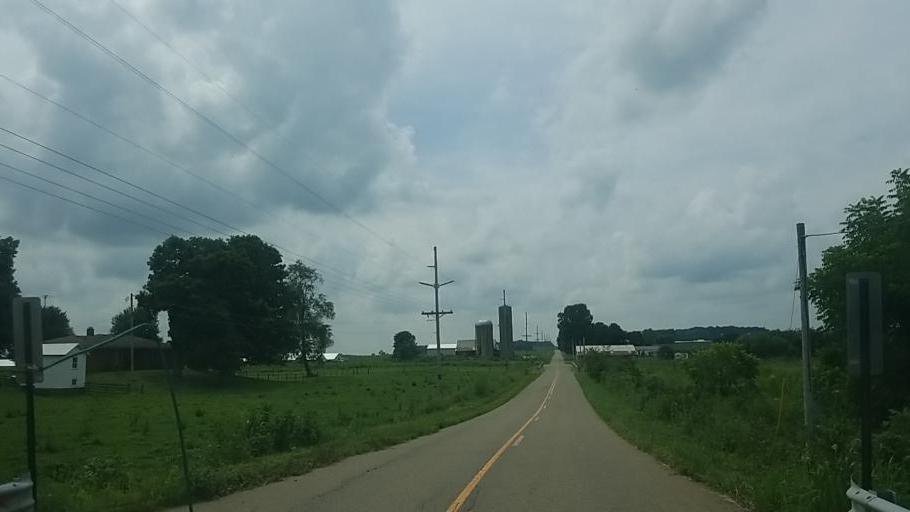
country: US
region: Ohio
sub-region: Knox County
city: Gambier
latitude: 40.3159
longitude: -82.3891
